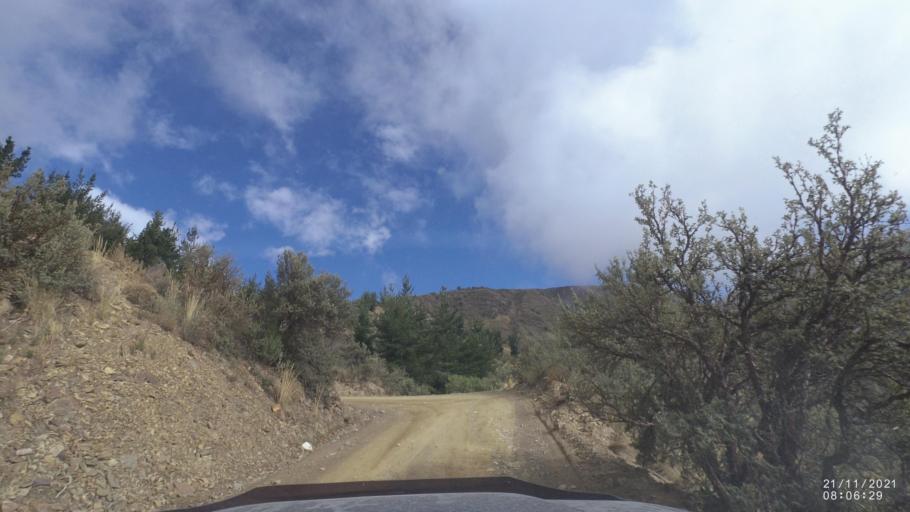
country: BO
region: Cochabamba
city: Cochabamba
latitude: -17.2878
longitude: -66.2097
